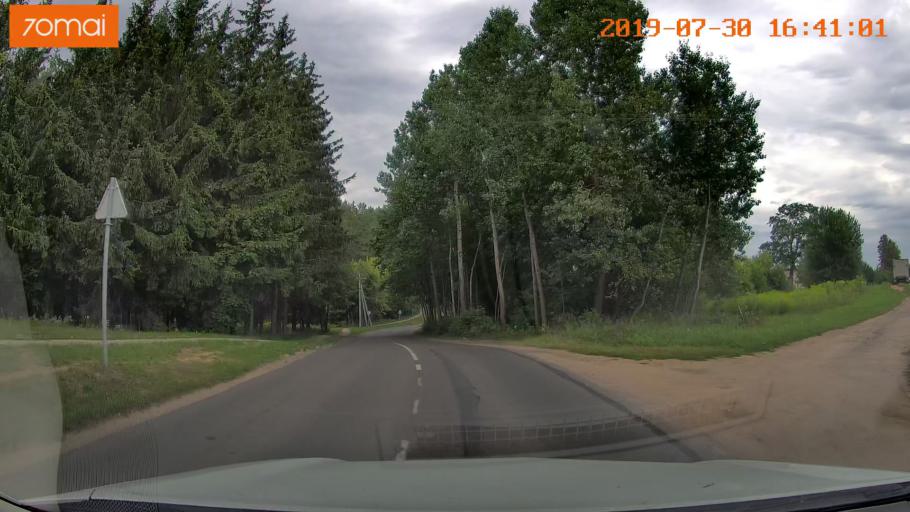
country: LT
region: Vilnius County
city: Rasos
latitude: 54.7083
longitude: 25.3584
